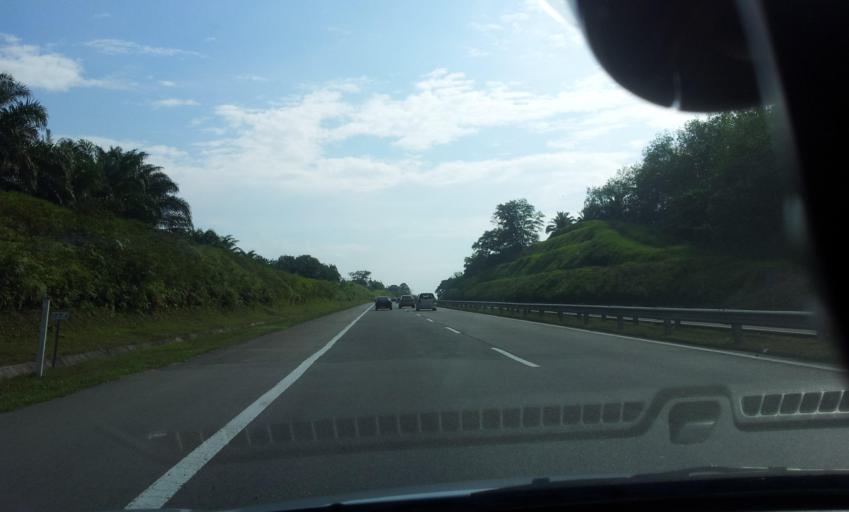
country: MY
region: Pahang
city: Mentekab
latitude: 3.5310
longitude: 102.2505
